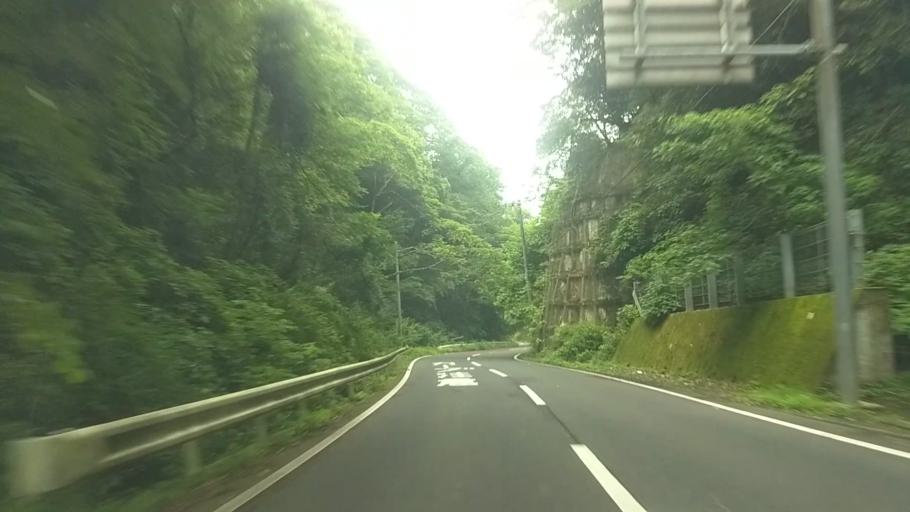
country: JP
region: Chiba
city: Kawaguchi
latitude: 35.2348
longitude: 140.0311
